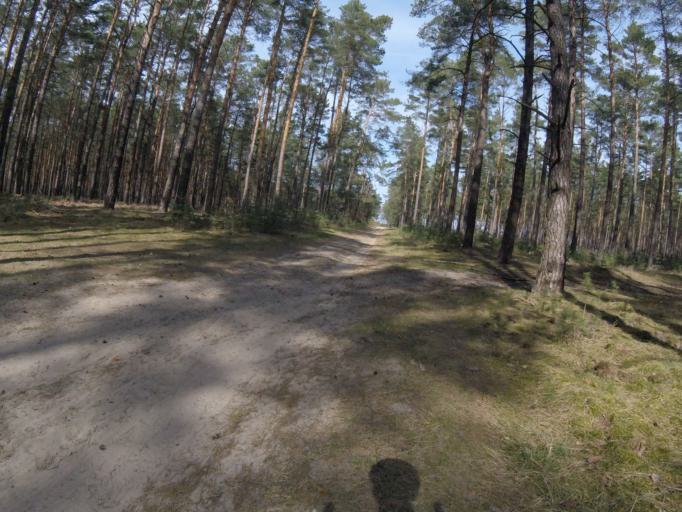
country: DE
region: Brandenburg
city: Bestensee
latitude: 52.2140
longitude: 13.6630
